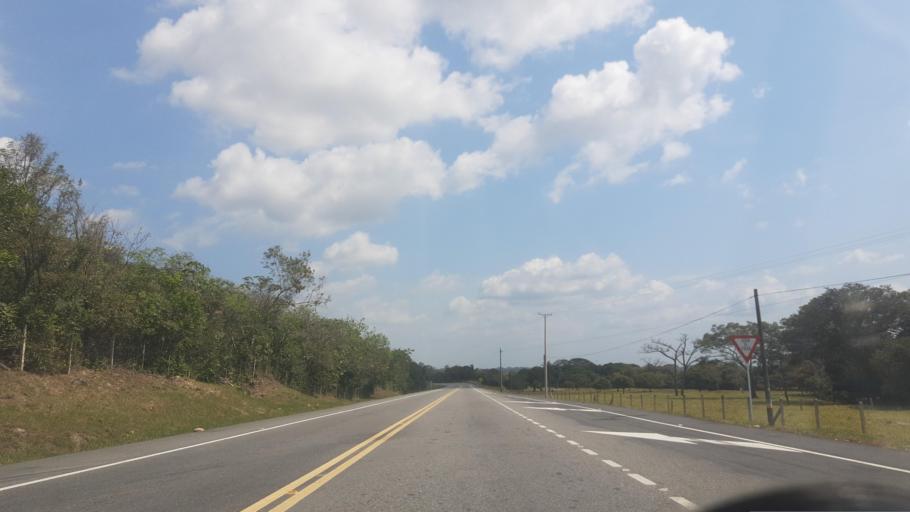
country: CO
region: Casanare
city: Tauramena
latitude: 4.8957
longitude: -72.6805
